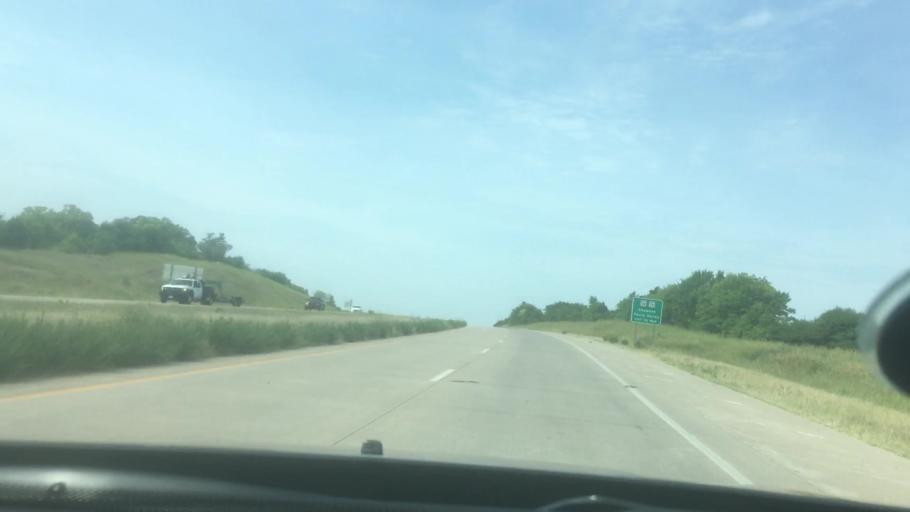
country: US
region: Oklahoma
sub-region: Pontotoc County
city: Ada
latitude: 34.7862
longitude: -96.6954
